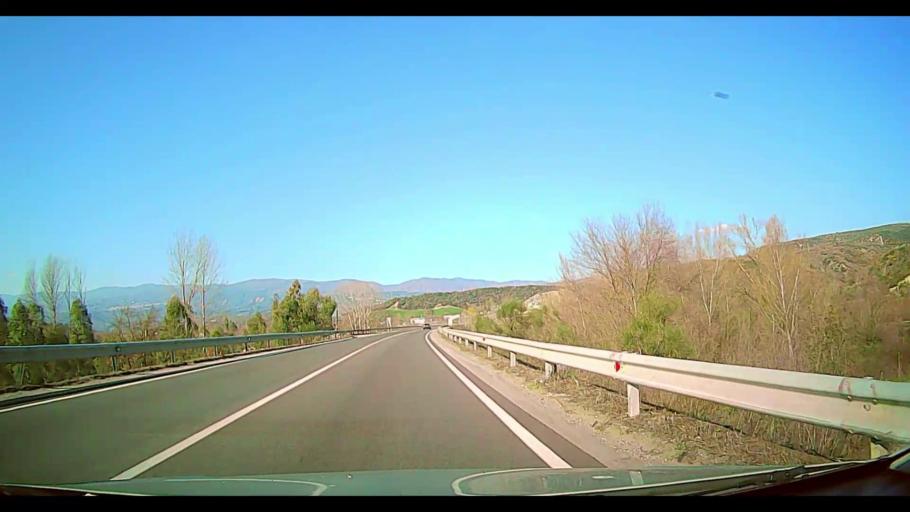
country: IT
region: Calabria
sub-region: Provincia di Crotone
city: Belvedere Spinello
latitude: 39.1878
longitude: 16.8555
